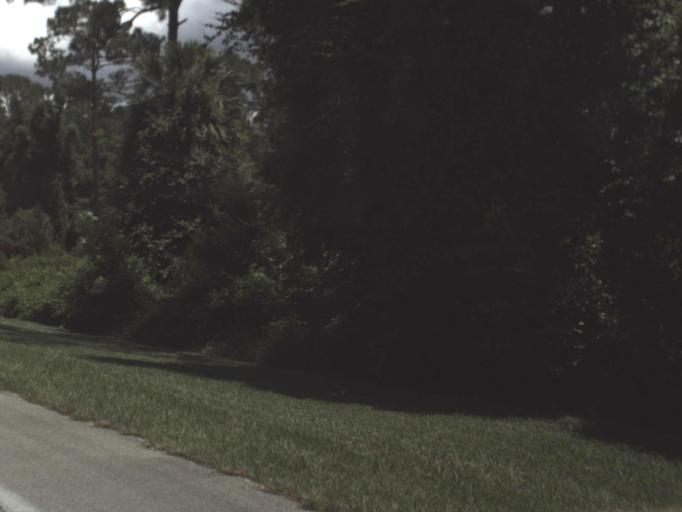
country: US
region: Florida
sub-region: Putnam County
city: Crescent City
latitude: 29.3932
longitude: -81.5089
